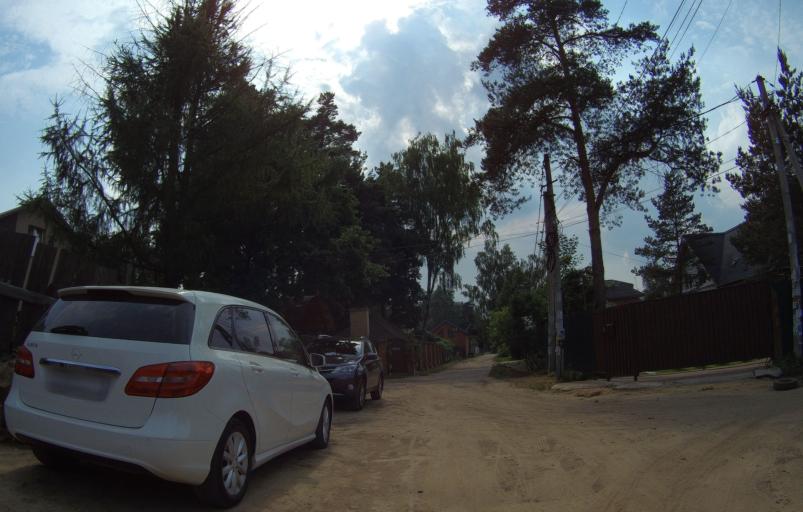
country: RU
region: Moskovskaya
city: Udel'naya
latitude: 55.6325
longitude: 38.0061
